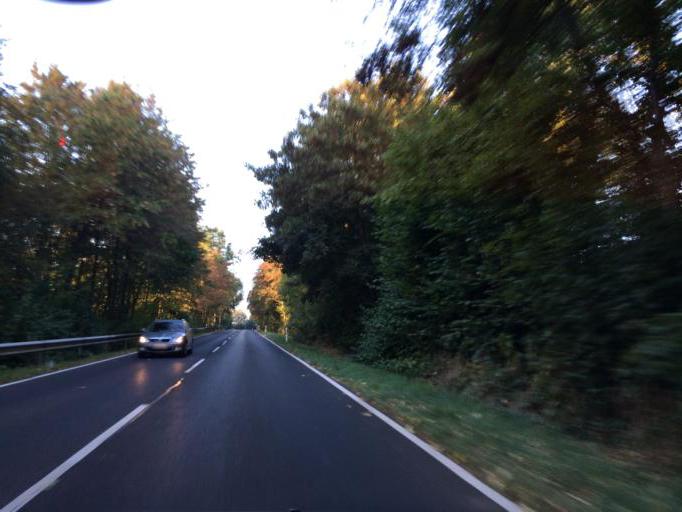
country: DE
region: North Rhine-Westphalia
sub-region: Regierungsbezirk Koln
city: Konigswinter
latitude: 50.6504
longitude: 7.1589
